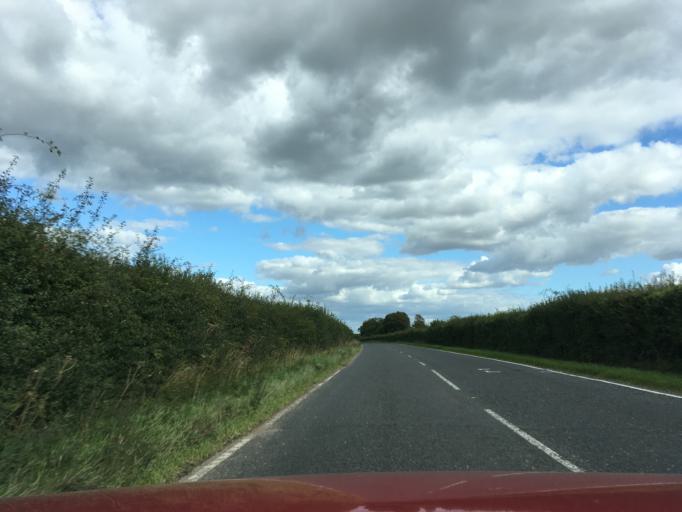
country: GB
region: England
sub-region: Hampshire
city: East Dean
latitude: 51.1115
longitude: -1.5912
